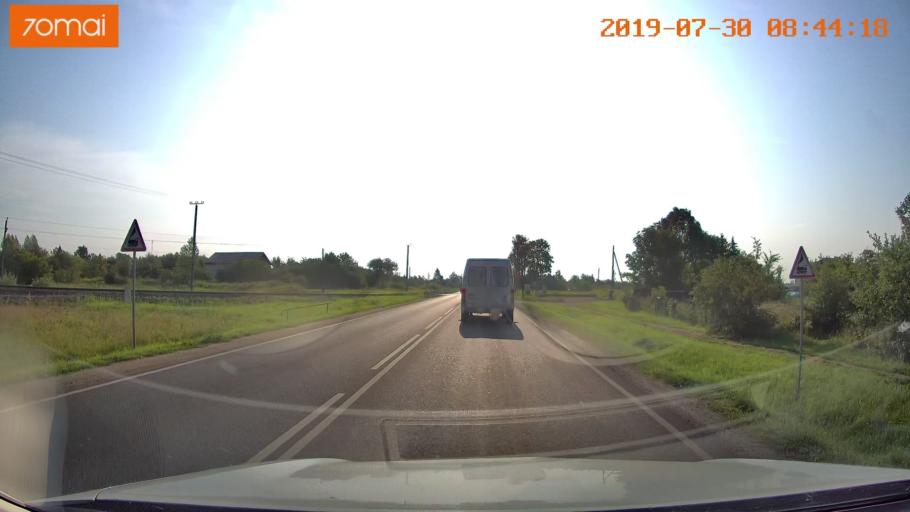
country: RU
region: Kaliningrad
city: Chernyakhovsk
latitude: 54.6265
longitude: 21.8556
